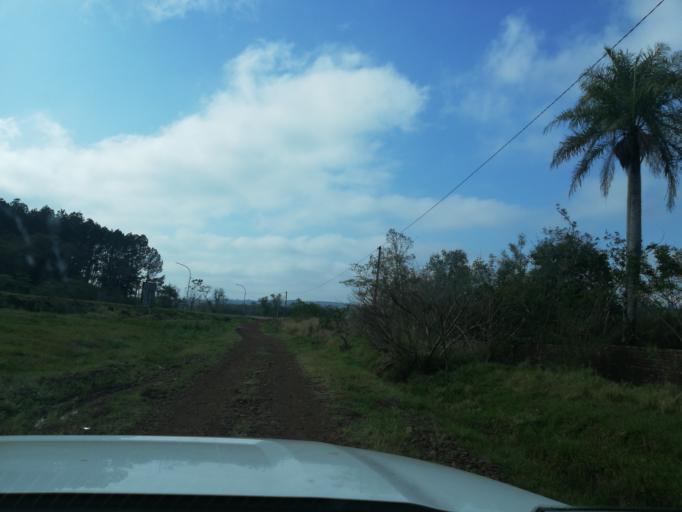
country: AR
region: Misiones
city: Cerro Azul
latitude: -27.5698
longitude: -55.4986
